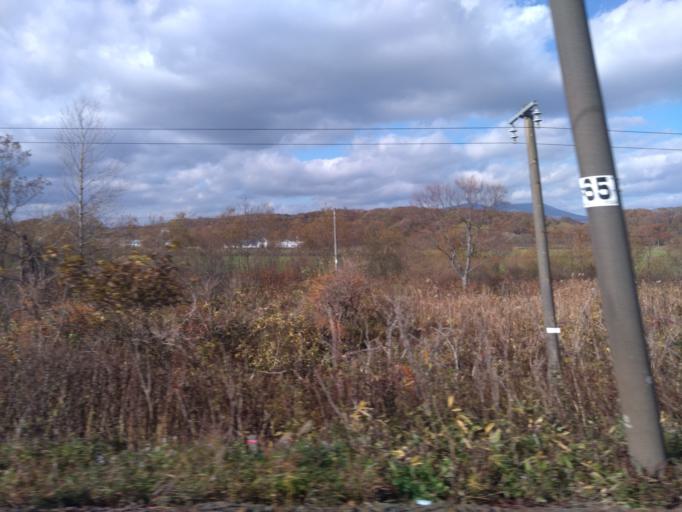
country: JP
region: Hokkaido
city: Shiraoi
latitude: 42.5723
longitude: 141.3980
